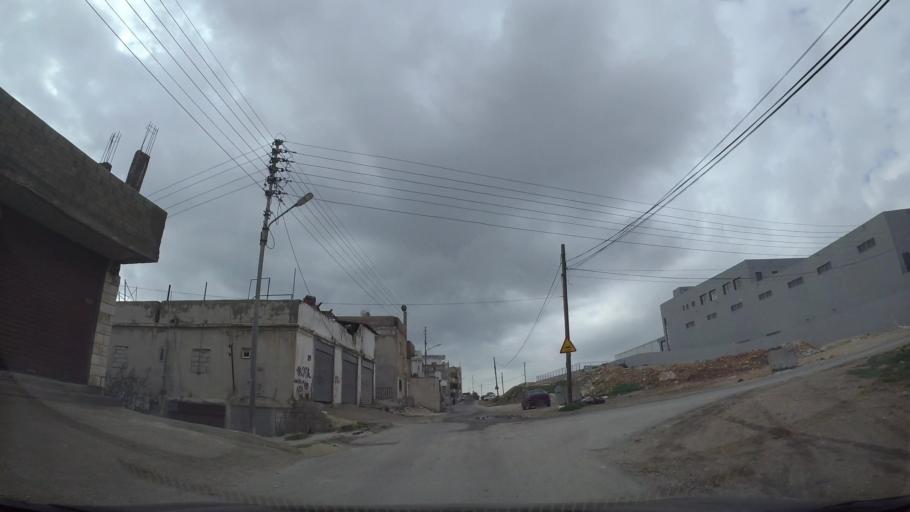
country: JO
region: Amman
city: Wadi as Sir
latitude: 31.9376
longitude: 35.8414
